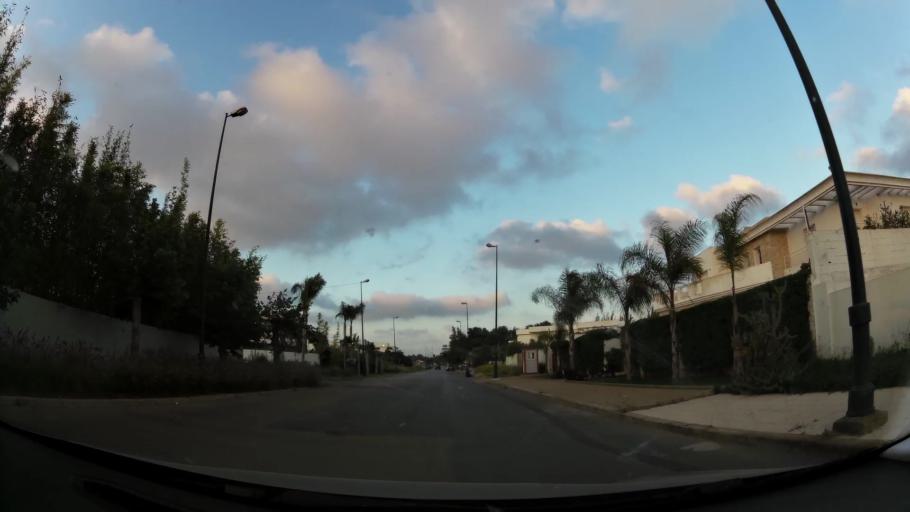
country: MA
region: Rabat-Sale-Zemmour-Zaer
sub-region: Rabat
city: Rabat
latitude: 33.9695
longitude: -6.8331
